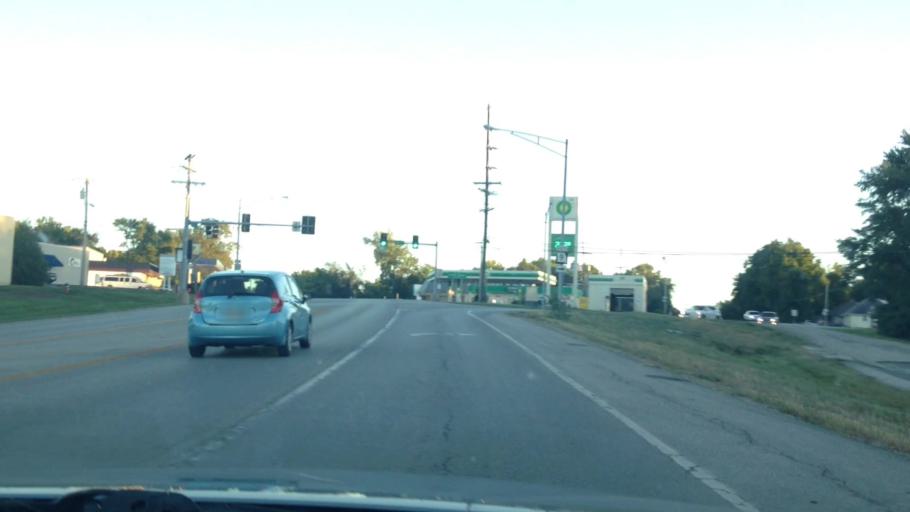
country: US
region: Missouri
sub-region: Platte County
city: Weatherby Lake
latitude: 39.2336
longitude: -94.6588
